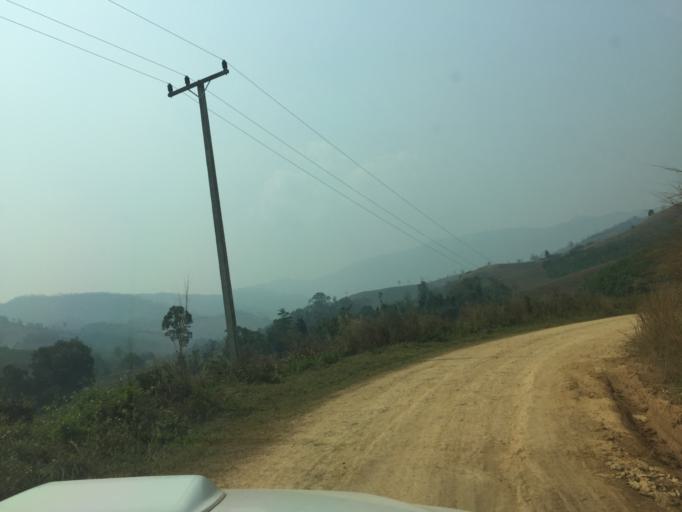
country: TH
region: Phayao
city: Phu Sang
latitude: 19.5916
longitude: 100.5268
